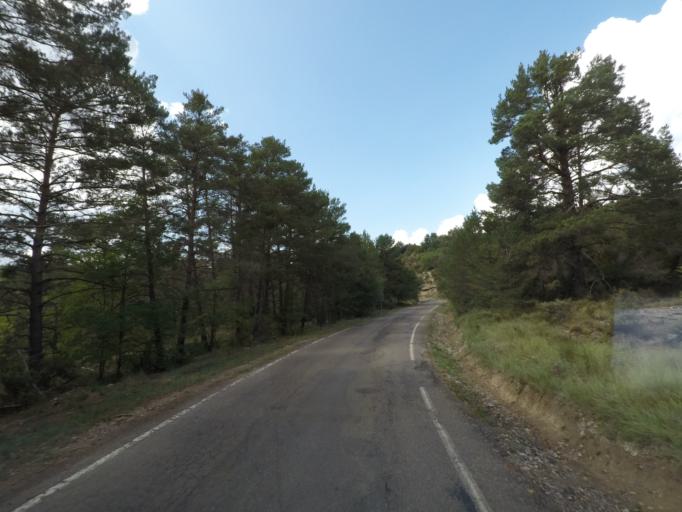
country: ES
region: Aragon
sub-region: Provincia de Huesca
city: Yebra de Basa
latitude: 42.3904
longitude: -0.3135
